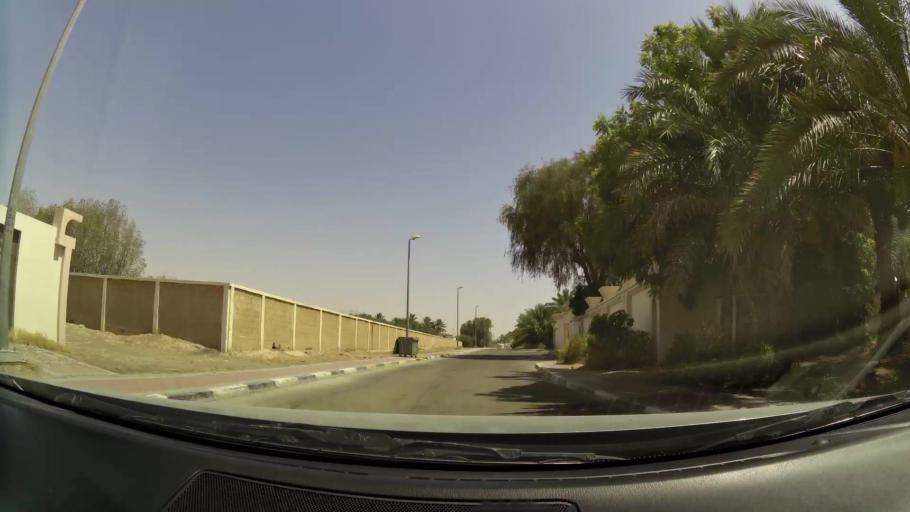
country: OM
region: Al Buraimi
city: Al Buraymi
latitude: 24.2762
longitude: 55.7806
